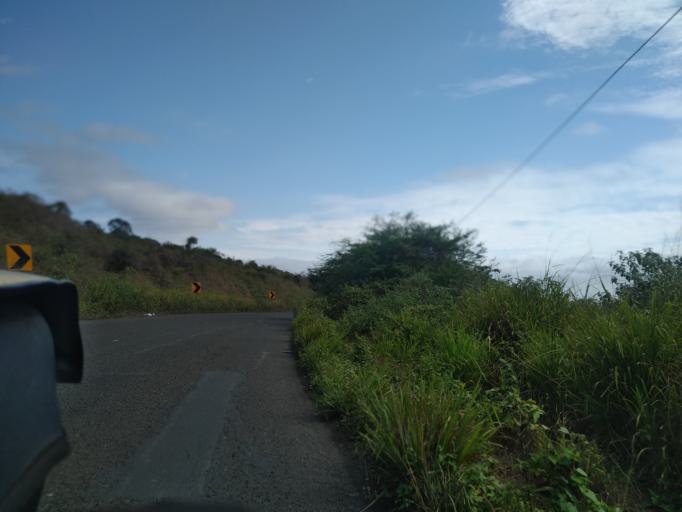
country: EC
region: Manabi
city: Jipijapa
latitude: -1.4416
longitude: -80.7535
